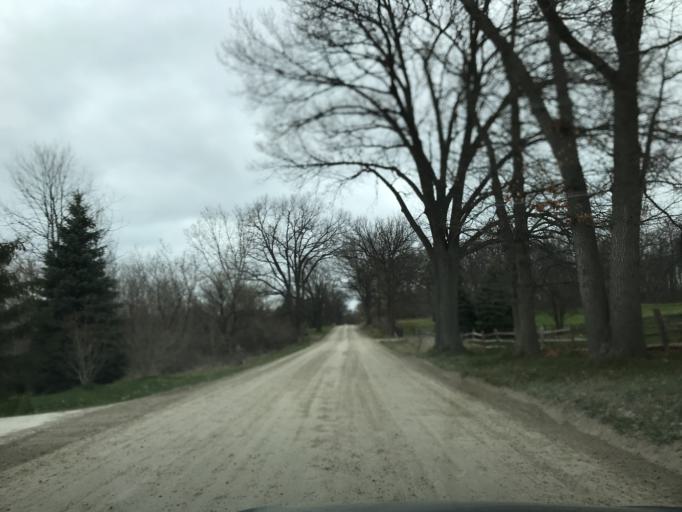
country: US
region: Michigan
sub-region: Oakland County
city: South Lyon
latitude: 42.4988
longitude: -83.6693
